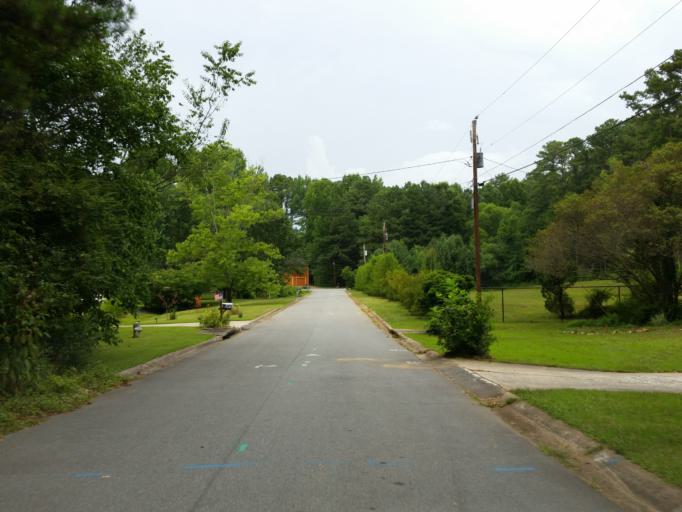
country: US
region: Georgia
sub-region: Cherokee County
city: Woodstock
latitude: 34.0236
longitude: -84.4760
